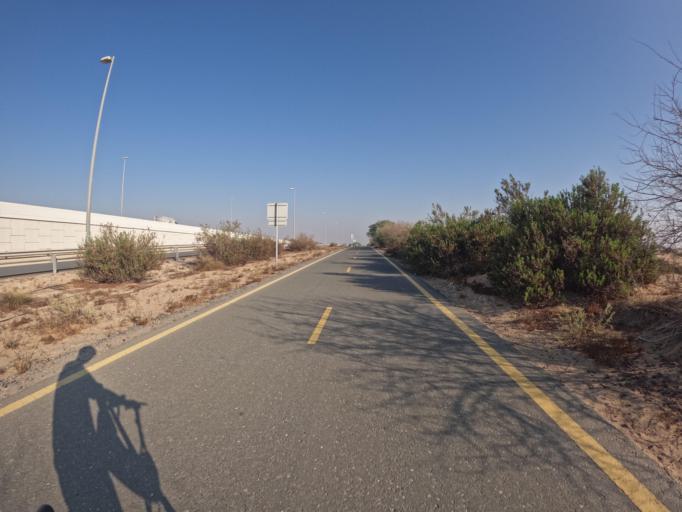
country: AE
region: Dubai
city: Dubai
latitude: 24.8968
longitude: 55.3419
